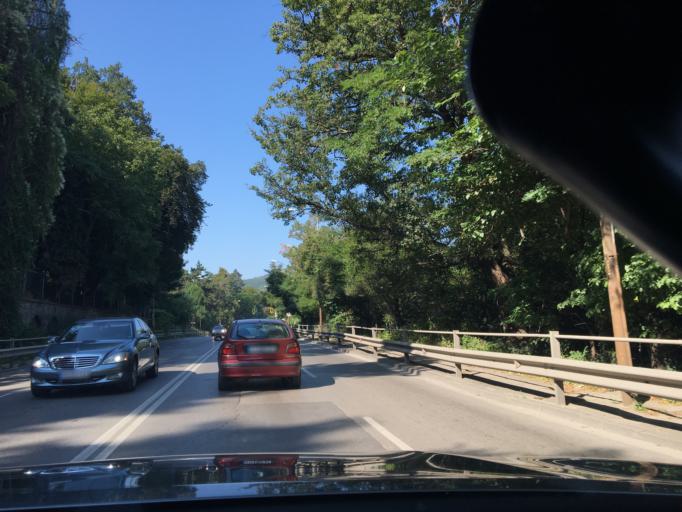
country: BG
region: Sofiya
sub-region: Obshtina Bozhurishte
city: Bozhurishte
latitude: 42.6547
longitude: 23.2293
